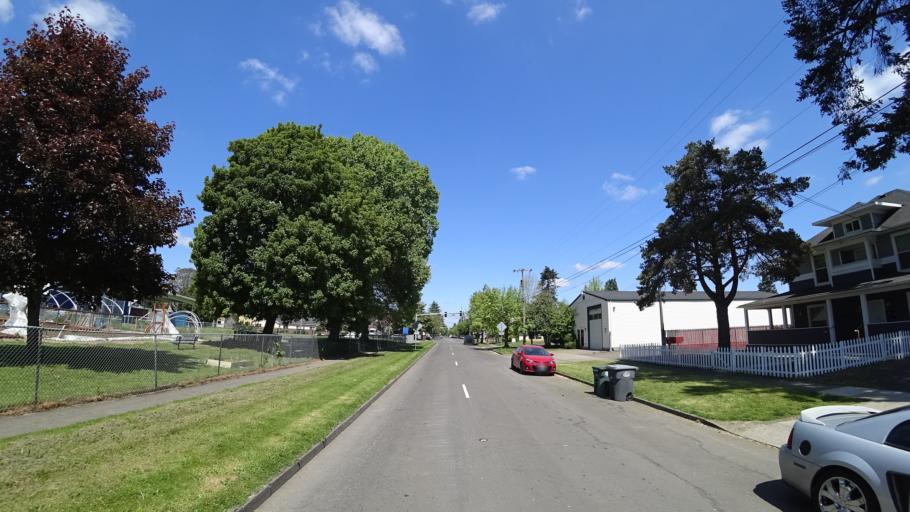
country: US
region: Oregon
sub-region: Washington County
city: Hillsboro
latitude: 45.5179
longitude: -122.9827
